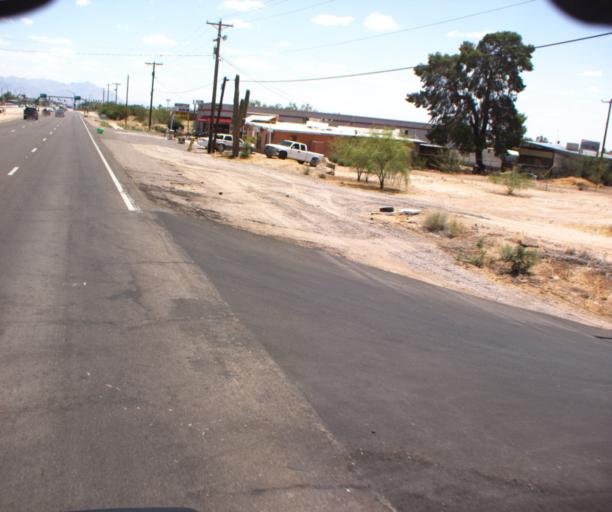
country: US
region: Arizona
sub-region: Pinal County
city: Apache Junction
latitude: 33.4151
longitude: -111.6420
